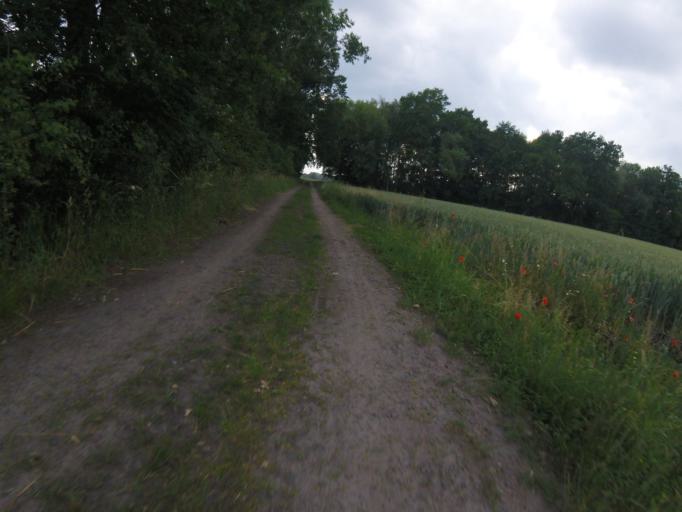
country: DE
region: Brandenburg
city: Mittenwalde
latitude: 52.2831
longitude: 13.5842
